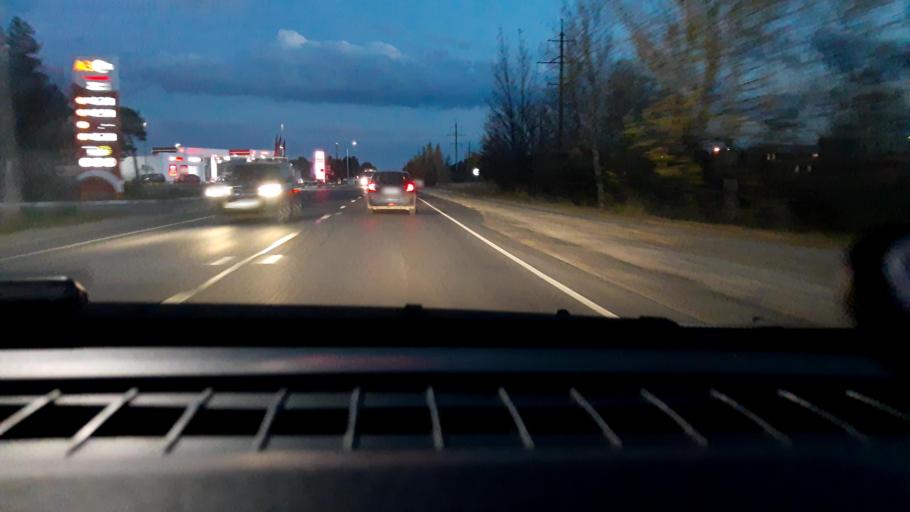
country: RU
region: Nizjnij Novgorod
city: Novaya Balakhna
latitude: 56.4784
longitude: 43.6056
